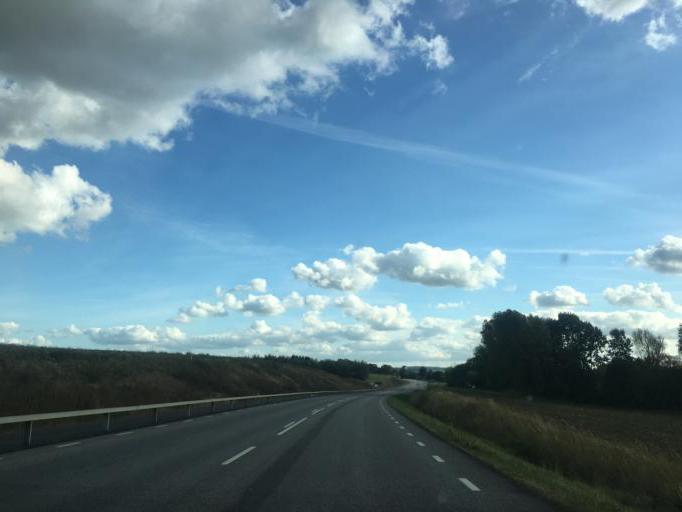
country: SE
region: Skane
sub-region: Eslovs Kommun
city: Eslov
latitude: 55.7674
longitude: 13.3221
